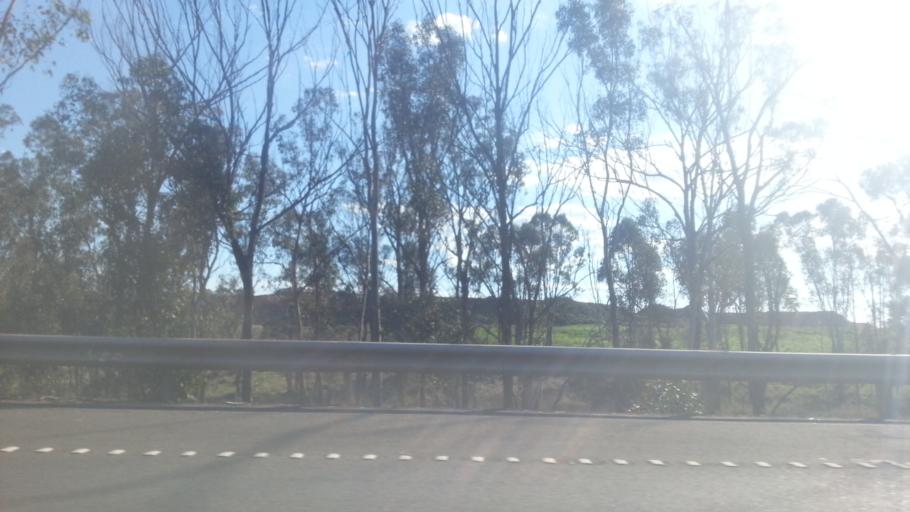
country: AU
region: New South Wales
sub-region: Hawkesbury
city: South Windsor
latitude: -33.6312
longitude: 150.7770
